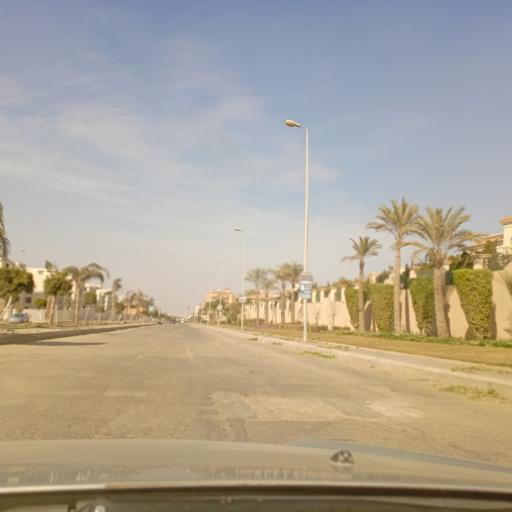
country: EG
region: Muhafazat al Qalyubiyah
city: Al Khankah
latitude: 30.0302
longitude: 31.4851
